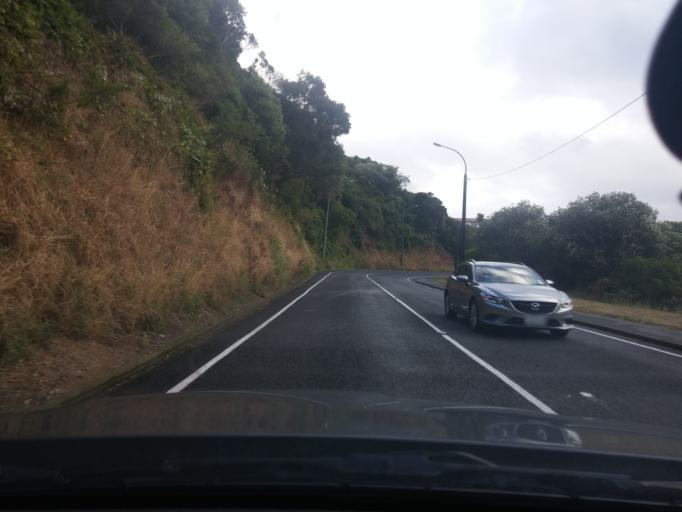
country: NZ
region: Wellington
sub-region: Wellington City
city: Kelburn
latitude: -41.2613
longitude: 174.7641
